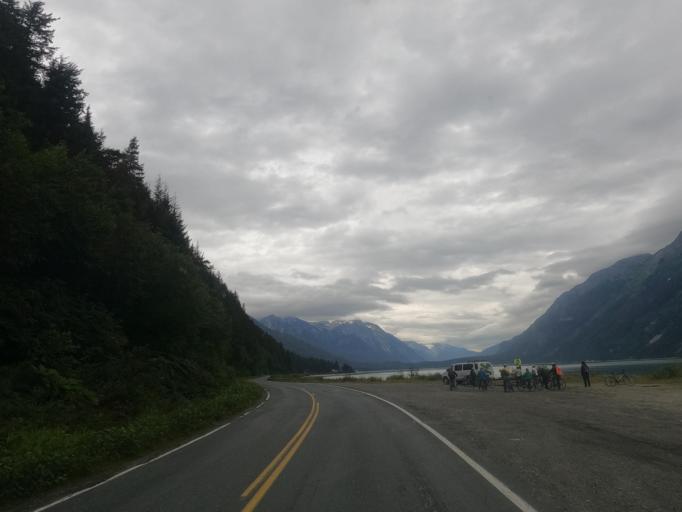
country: US
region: Alaska
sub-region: Haines Borough
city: Haines
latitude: 59.2909
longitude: -135.4943
